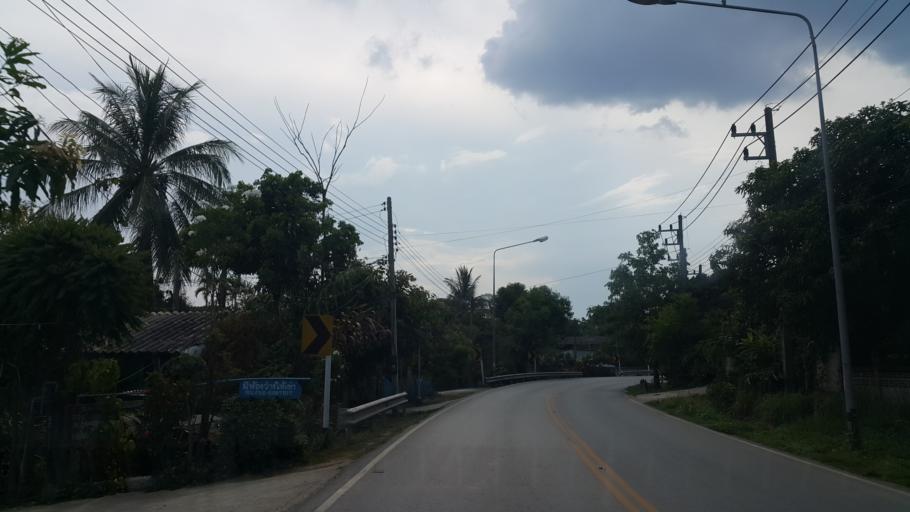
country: TH
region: Chiang Rai
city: Chiang Rai
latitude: 19.9106
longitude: 99.8784
